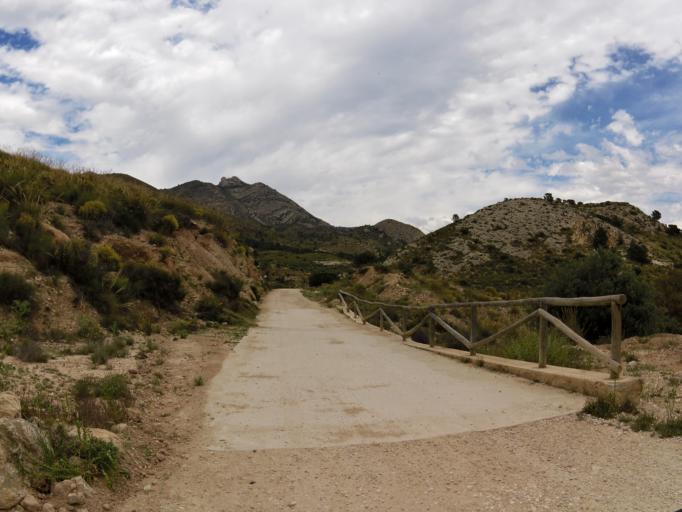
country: ES
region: Valencia
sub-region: Provincia de Alicante
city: Agost
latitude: 38.4771
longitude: -0.6451
